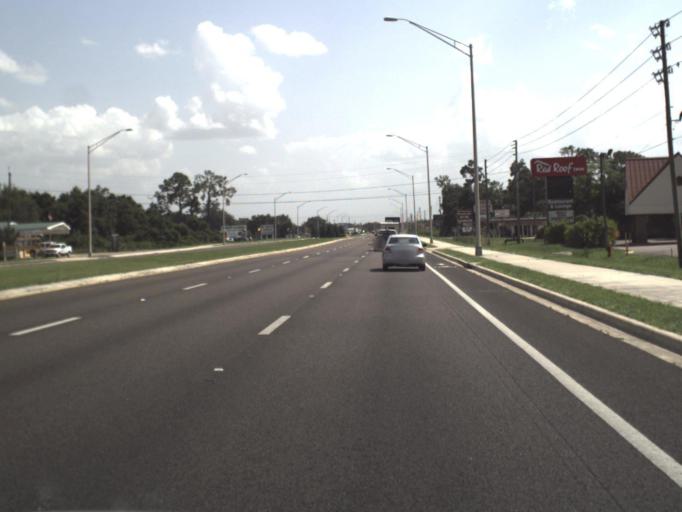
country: US
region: Florida
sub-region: Polk County
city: Dundee
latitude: 28.0248
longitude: -81.6340
